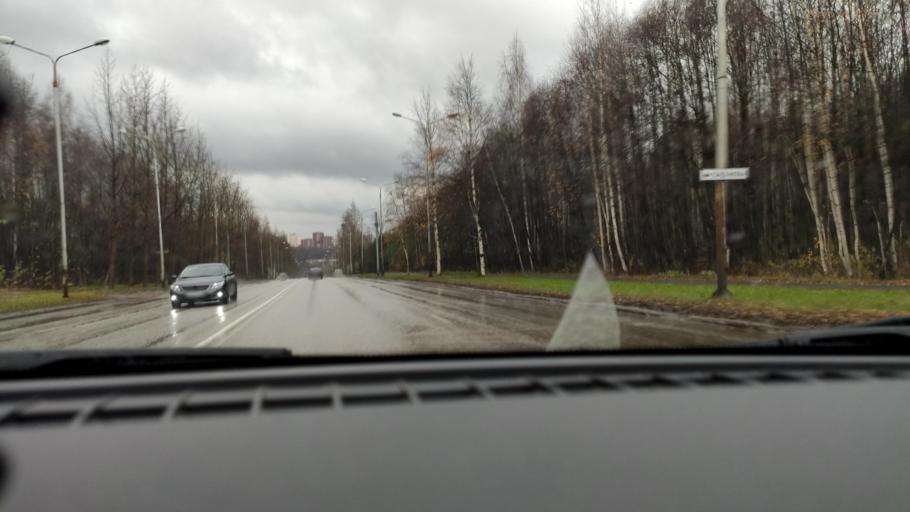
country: RU
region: Perm
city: Perm
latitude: 58.0785
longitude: 56.3719
